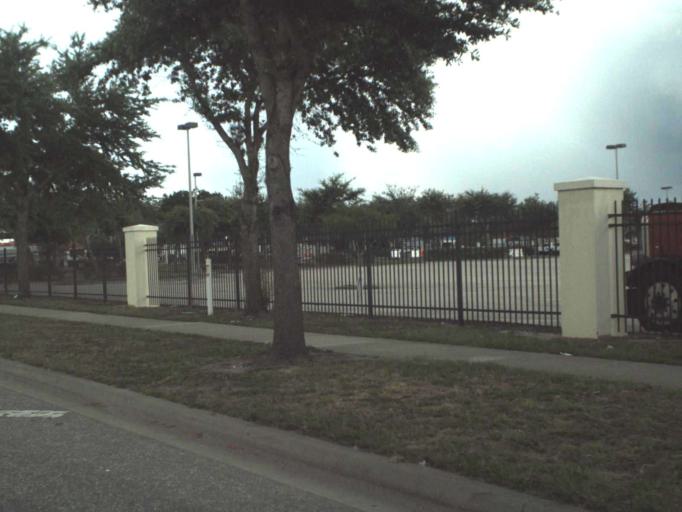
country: US
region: Florida
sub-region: Orange County
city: Orlando
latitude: 28.5512
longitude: -81.4136
